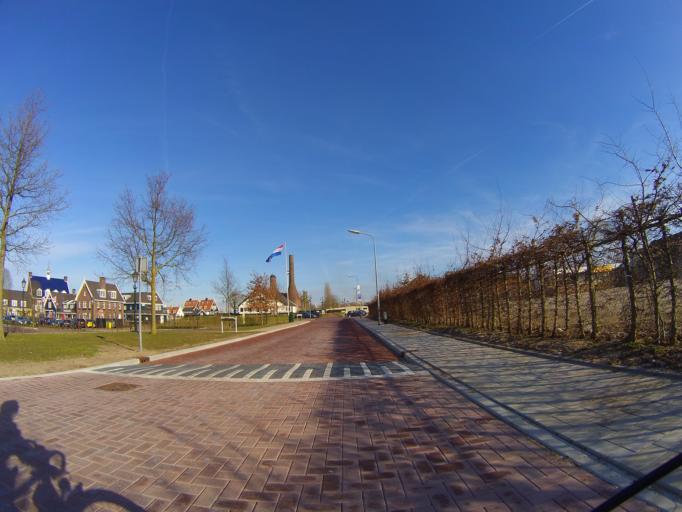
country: NL
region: North Holland
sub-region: Gemeente Huizen
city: Huizen
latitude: 52.3092
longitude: 5.2419
